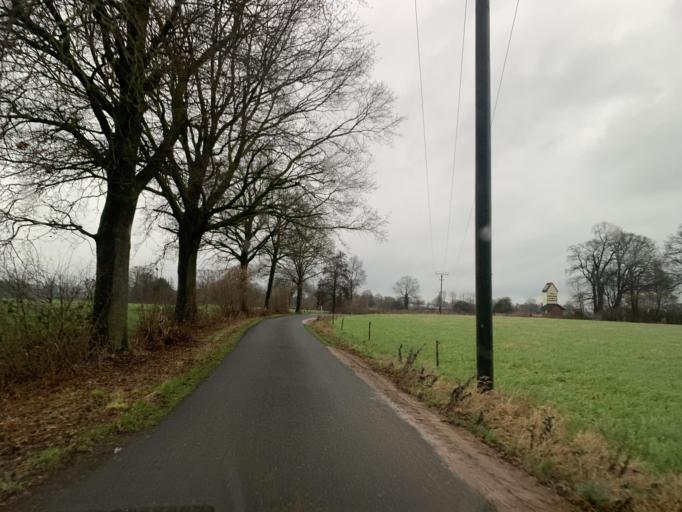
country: DE
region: North Rhine-Westphalia
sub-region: Regierungsbezirk Munster
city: Nordwalde
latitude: 52.0932
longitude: 7.5135
